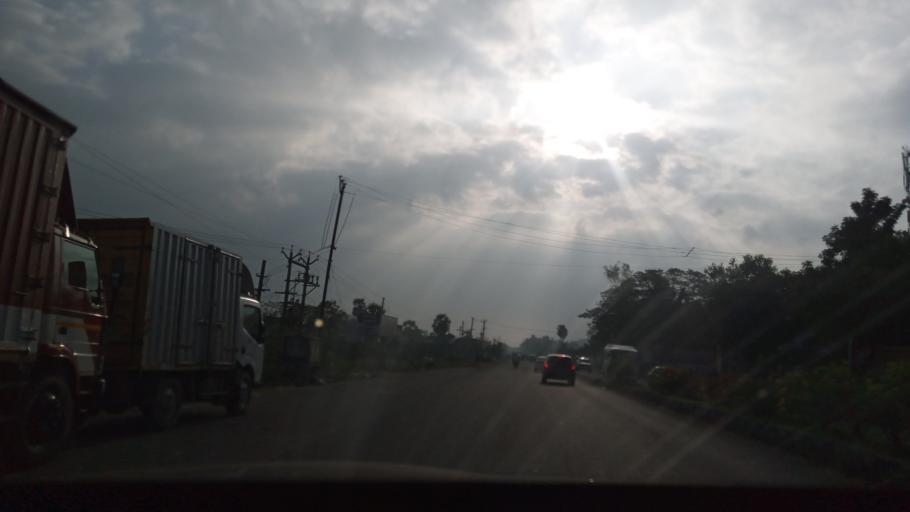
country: IN
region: Tamil Nadu
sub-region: Kancheepuram
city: Vandalur
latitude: 12.8674
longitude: 80.1151
